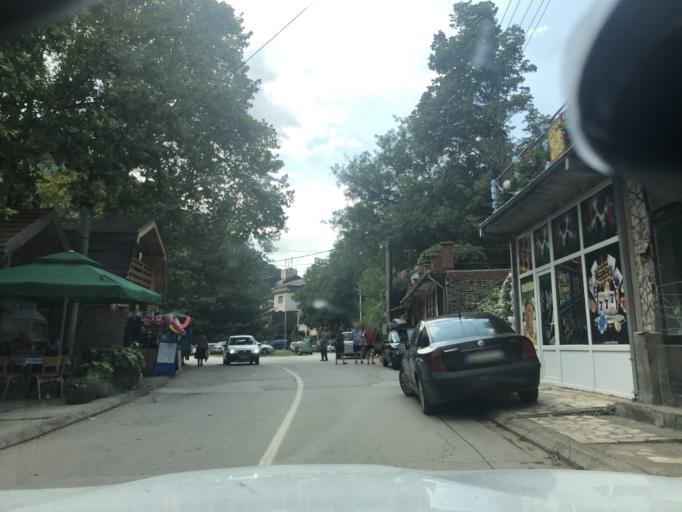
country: RS
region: Central Serbia
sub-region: Jablanicki Okrug
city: Medvega
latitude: 42.7769
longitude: 21.6045
